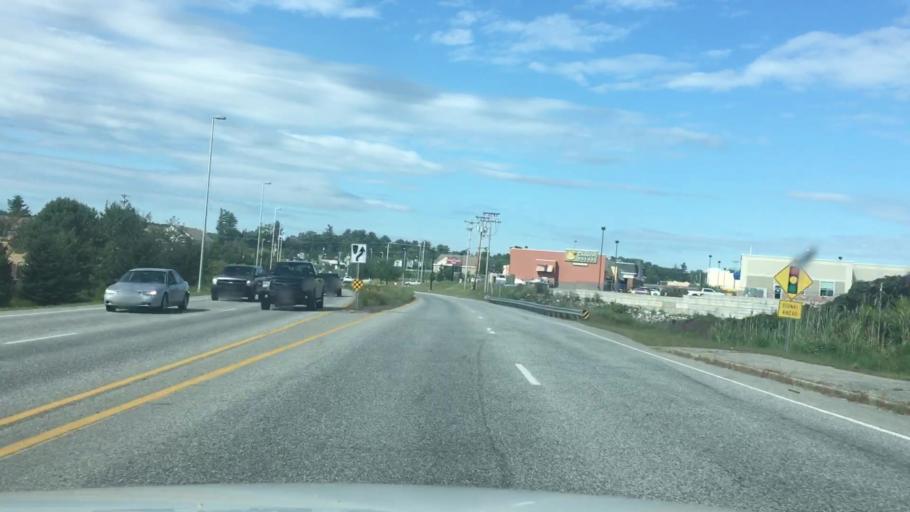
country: US
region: Maine
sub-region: Androscoggin County
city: Auburn
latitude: 44.1208
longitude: -70.2299
